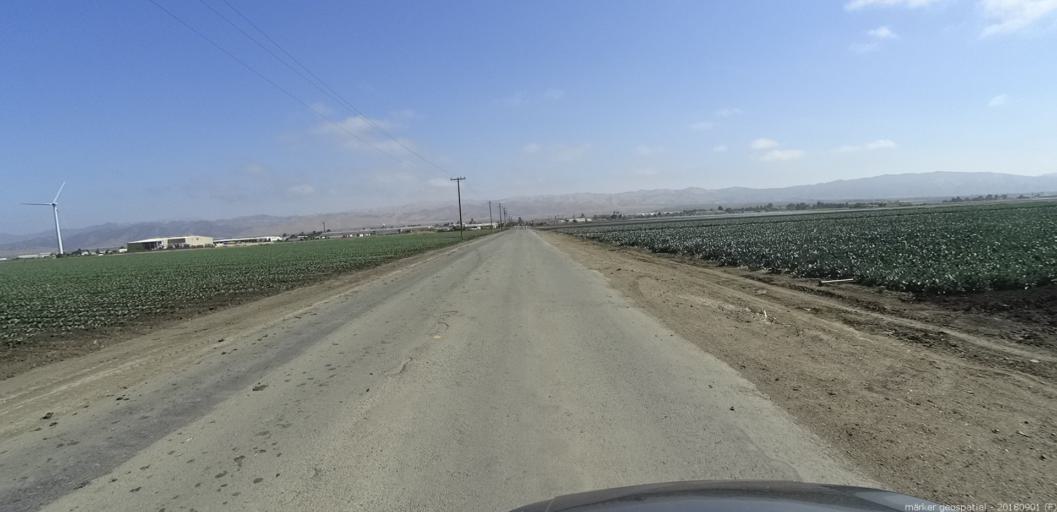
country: US
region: California
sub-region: Monterey County
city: Gonzales
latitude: 36.4964
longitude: -121.4530
